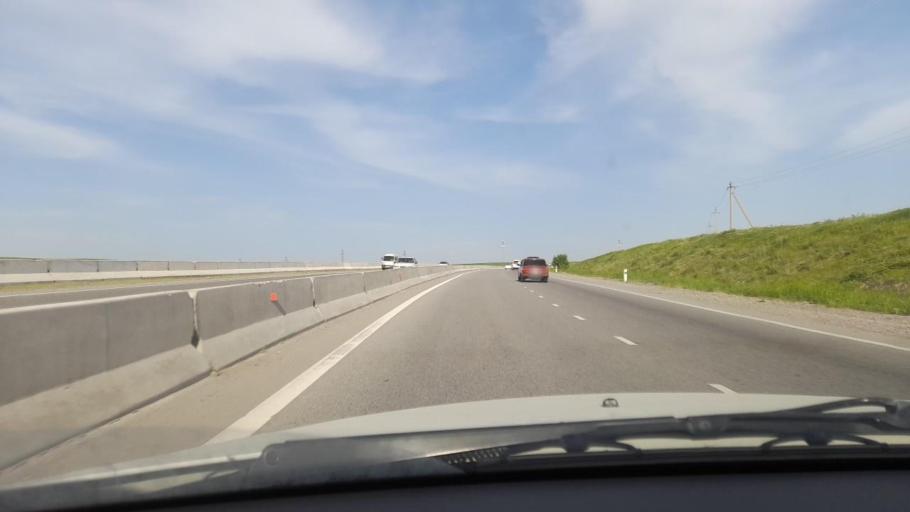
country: UZ
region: Jizzax
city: Jizzax
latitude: 40.0545
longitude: 67.7200
